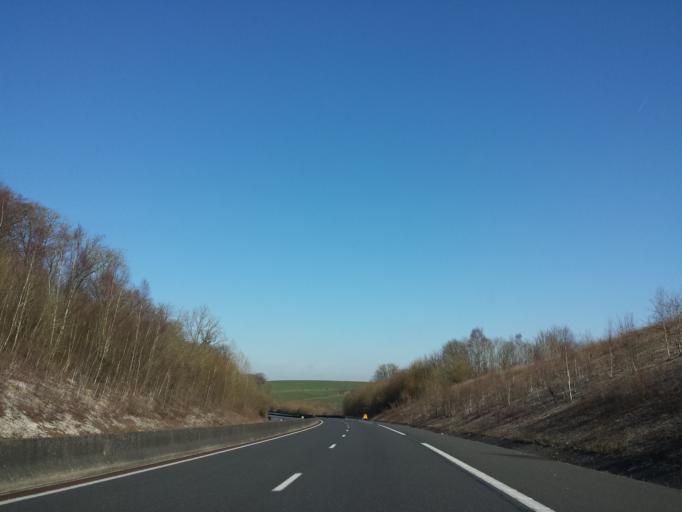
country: FR
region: Picardie
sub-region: Departement de l'Oise
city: Breteuil
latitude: 49.5773
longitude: 2.2038
